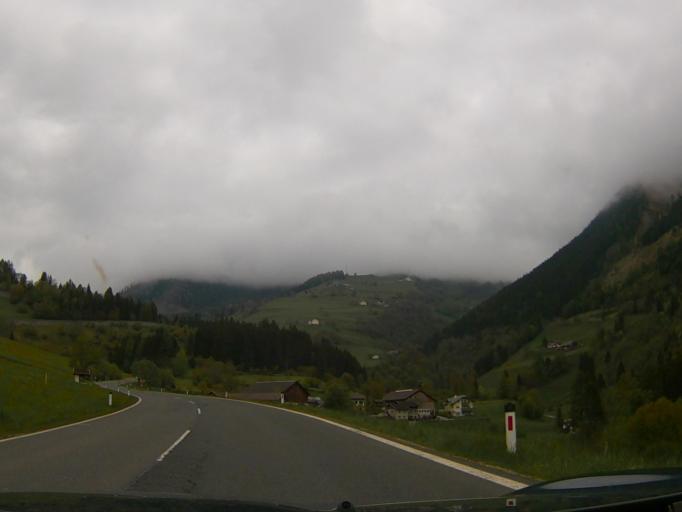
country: AT
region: Carinthia
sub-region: Politischer Bezirk Spittal an der Drau
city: Obervellach
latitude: 46.9616
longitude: 13.1852
